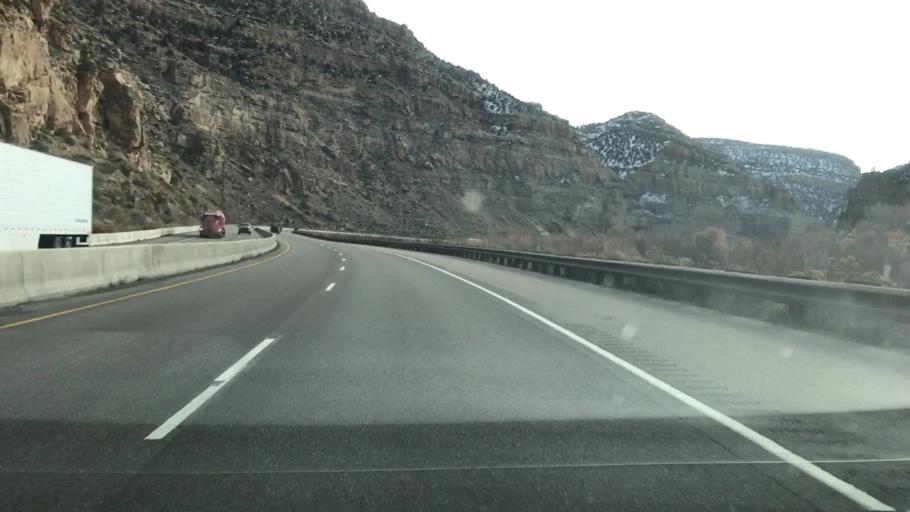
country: US
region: Colorado
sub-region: Mesa County
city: Palisade
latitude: 39.2284
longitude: -108.2631
